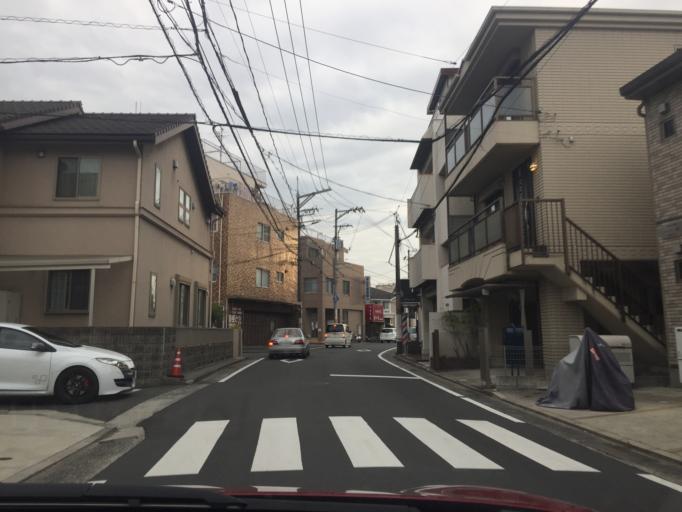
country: JP
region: Hiroshima
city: Hiroshima-shi
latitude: 34.4334
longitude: 132.4602
